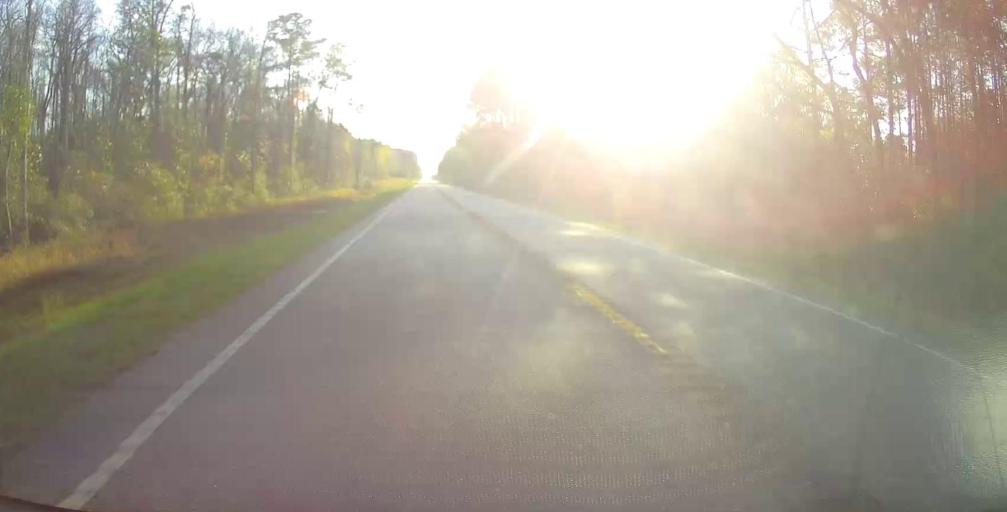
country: US
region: Georgia
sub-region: Tattnall County
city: Reidsville
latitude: 32.1390
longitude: -82.0361
